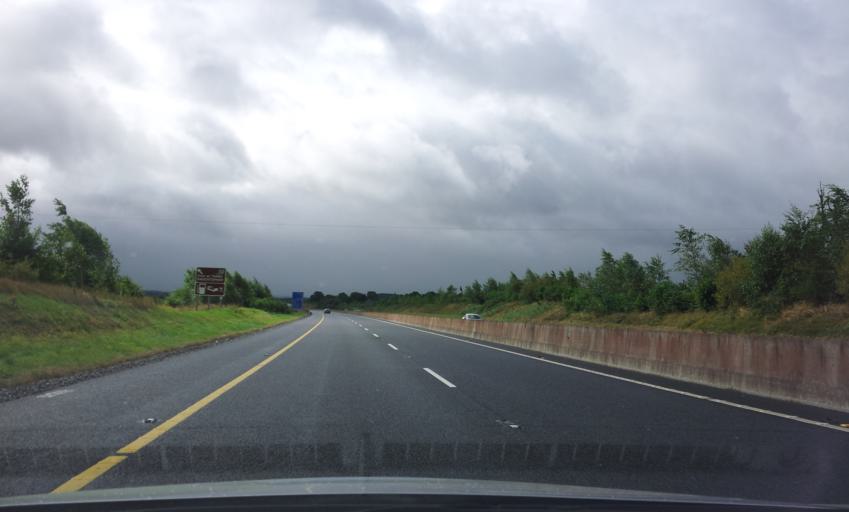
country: IE
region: Leinster
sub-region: Kilkenny
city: Thomastown
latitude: 52.5004
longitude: -7.2433
